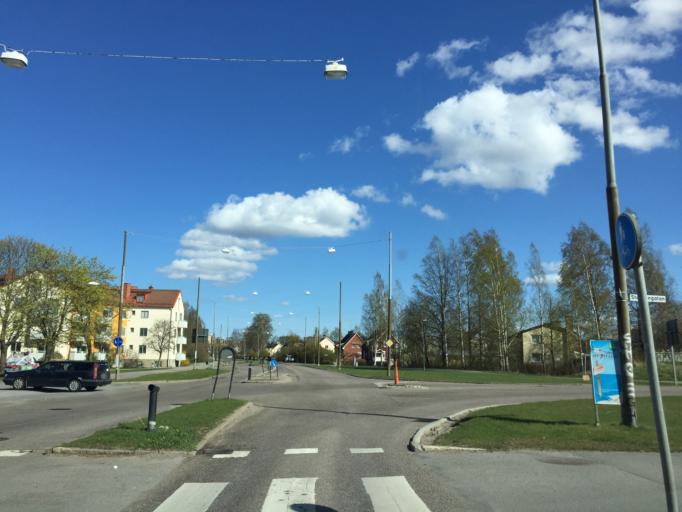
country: SE
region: OErebro
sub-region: Orebro Kommun
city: Orebro
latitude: 59.2693
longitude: 15.1798
